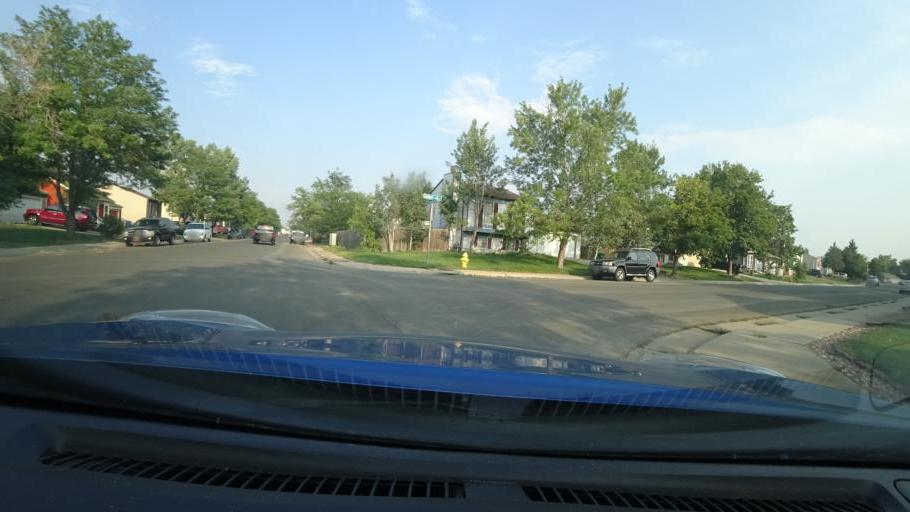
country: US
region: Colorado
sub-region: Adams County
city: Aurora
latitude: 39.7472
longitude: -104.7668
